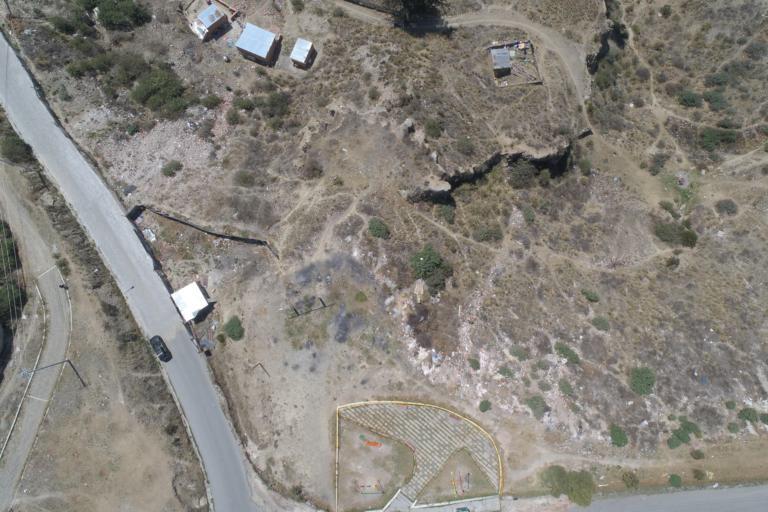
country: BO
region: La Paz
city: La Paz
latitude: -16.4998
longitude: -68.1006
